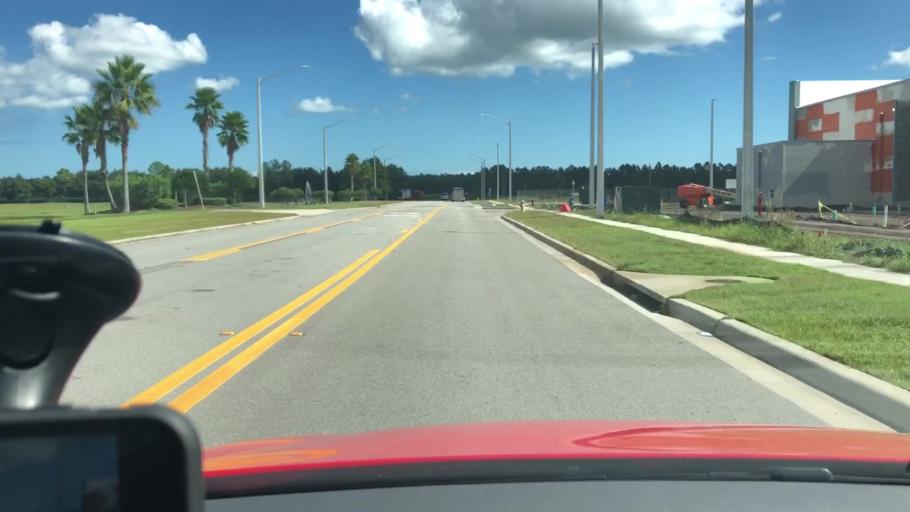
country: US
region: Florida
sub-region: Volusia County
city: Holly Hill
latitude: 29.2198
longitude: -81.0955
